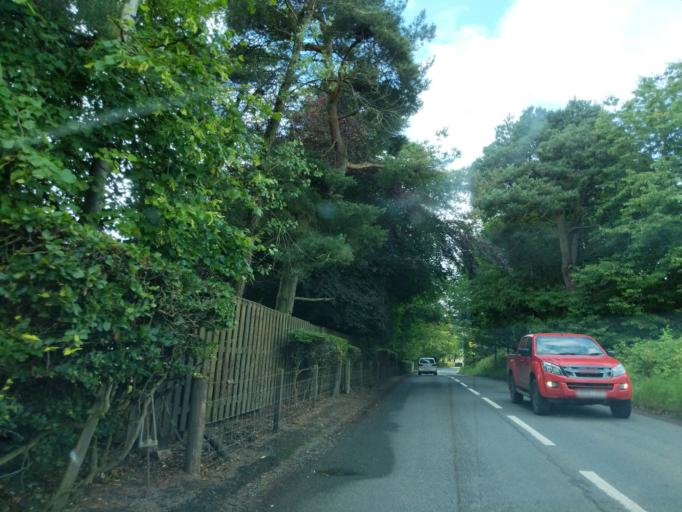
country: GB
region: Scotland
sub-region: South Lanarkshire
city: Biggar
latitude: 55.6046
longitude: -3.5937
